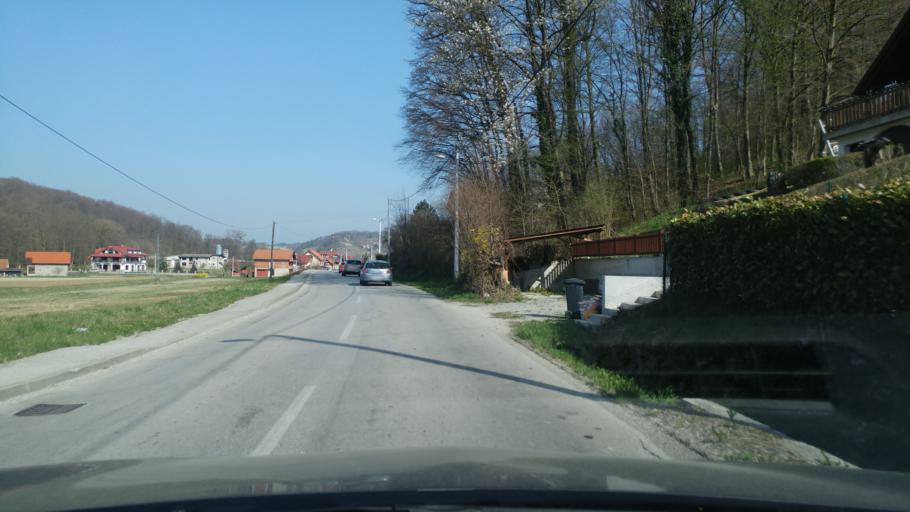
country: HR
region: Zagrebacka
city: Pojatno
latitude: 45.9037
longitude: 15.7821
